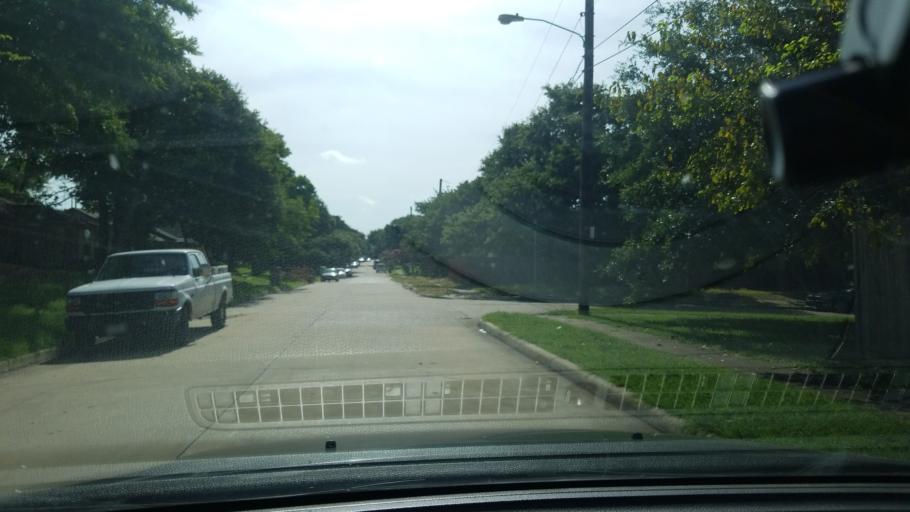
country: US
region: Texas
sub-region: Dallas County
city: Balch Springs
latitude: 32.7286
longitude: -96.6472
